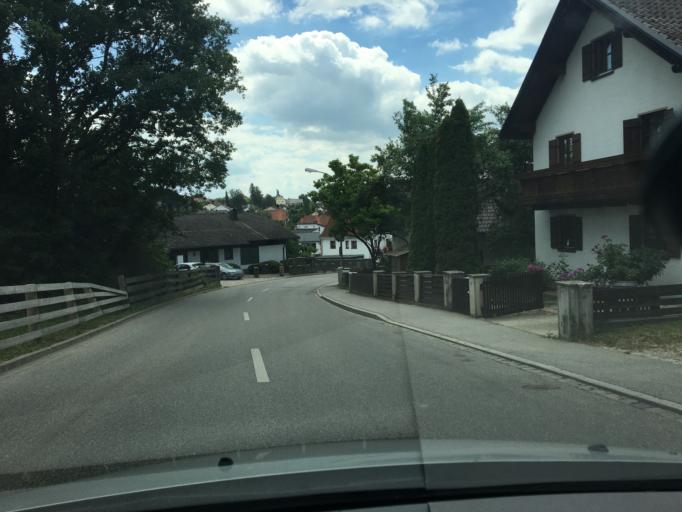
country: DE
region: Bavaria
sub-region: Lower Bavaria
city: Vilsbiburg
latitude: 48.4499
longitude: 12.3663
